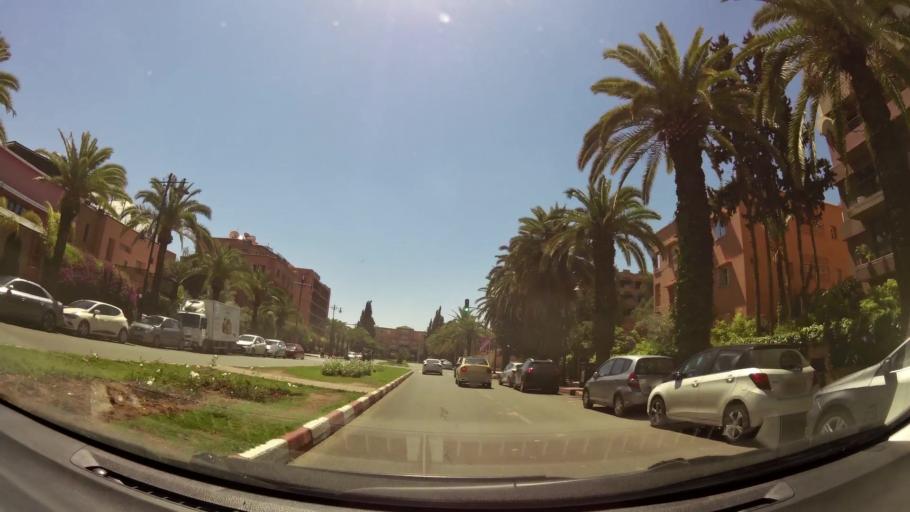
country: MA
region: Marrakech-Tensift-Al Haouz
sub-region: Marrakech
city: Marrakesh
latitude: 31.6239
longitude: -8.0034
